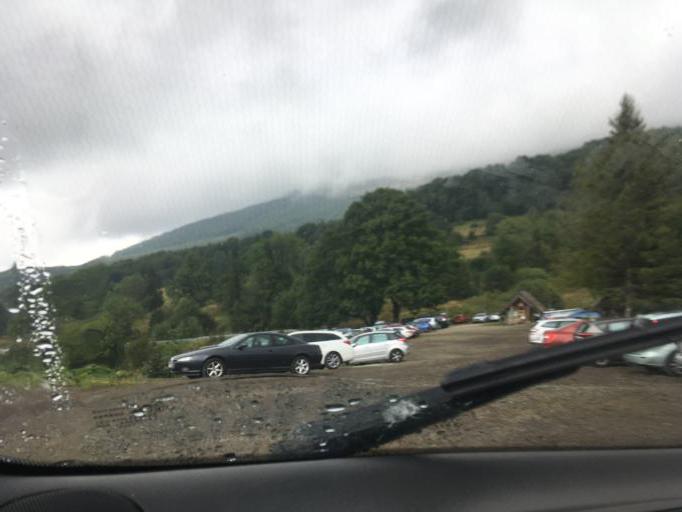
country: PL
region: Subcarpathian Voivodeship
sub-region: Powiat bieszczadzki
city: Lutowiska
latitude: 49.1244
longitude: 22.5911
